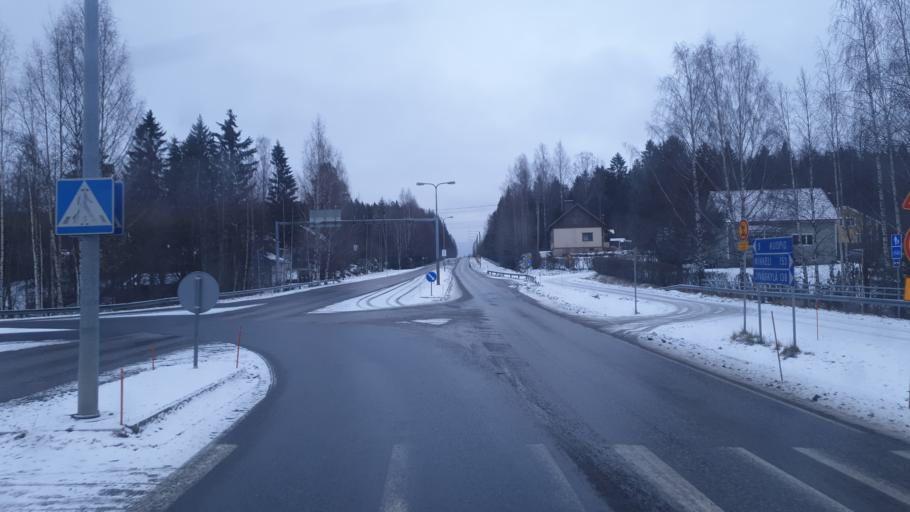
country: FI
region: Northern Savo
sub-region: Kuopio
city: Kuopio
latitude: 62.8390
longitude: 27.6115
